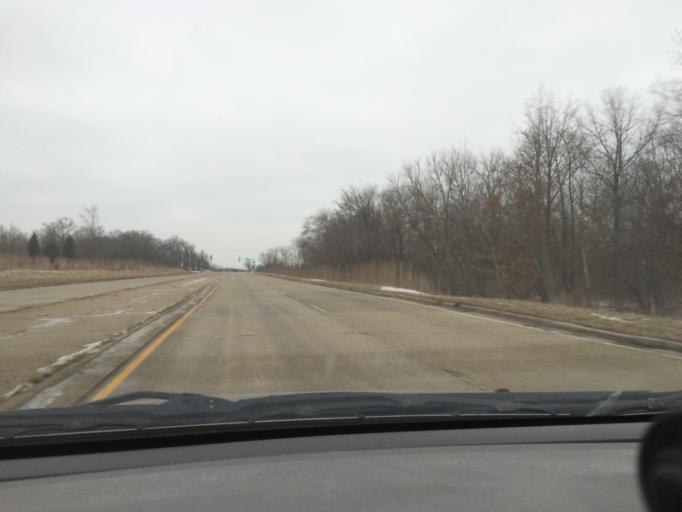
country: US
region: Illinois
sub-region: Cook County
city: Streamwood
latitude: 42.0416
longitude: -88.1791
